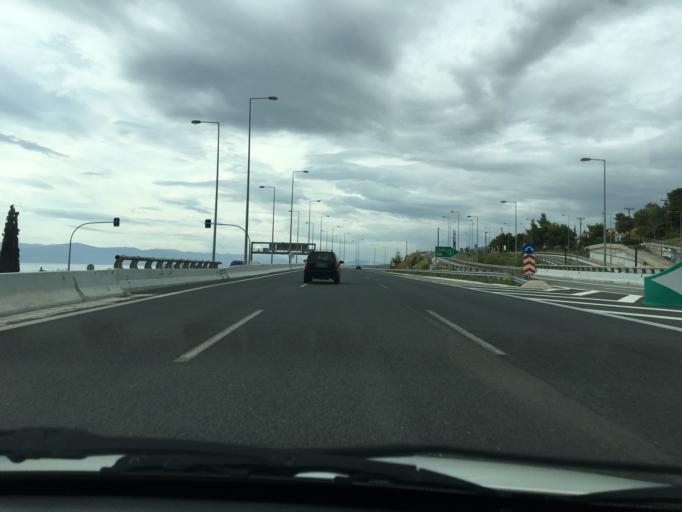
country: GR
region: Attica
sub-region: Nomarchia Dytikis Attikis
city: Kineta
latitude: 37.9758
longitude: 23.2316
